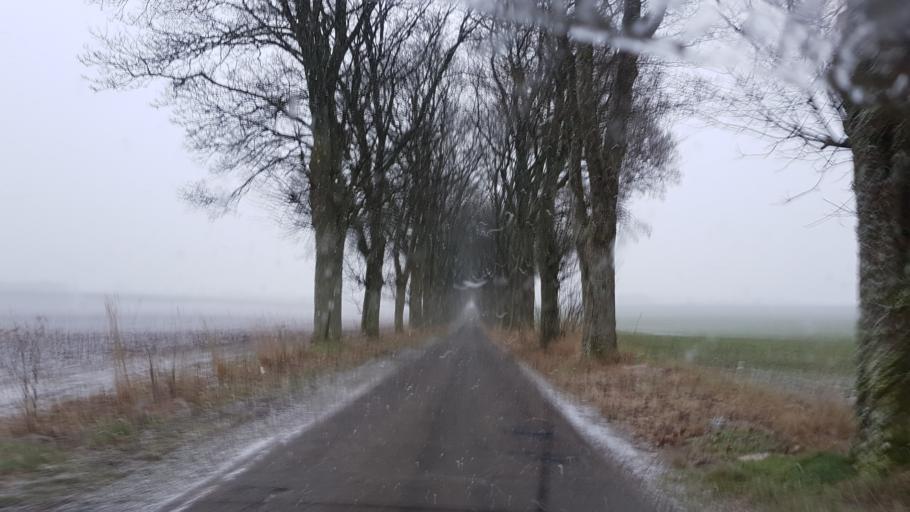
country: PL
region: West Pomeranian Voivodeship
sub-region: Powiat slawienski
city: Slawno
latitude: 54.2803
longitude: 16.6087
